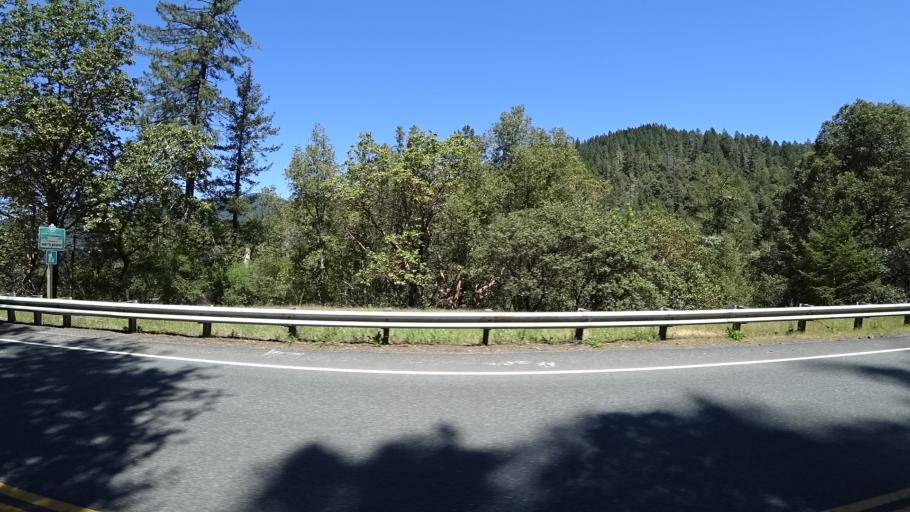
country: US
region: California
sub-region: Humboldt County
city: Willow Creek
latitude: 40.8644
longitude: -123.5159
